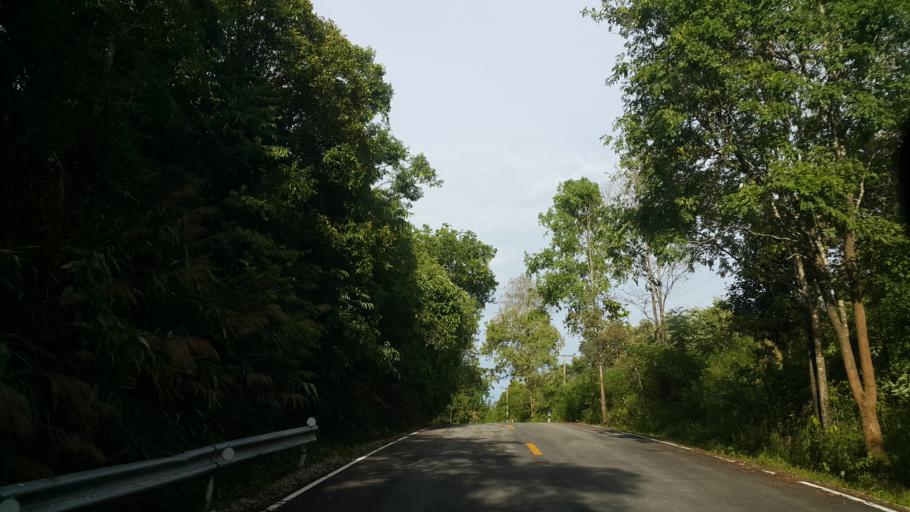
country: TH
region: Loei
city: Na Haeo
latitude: 17.5240
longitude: 101.0046
